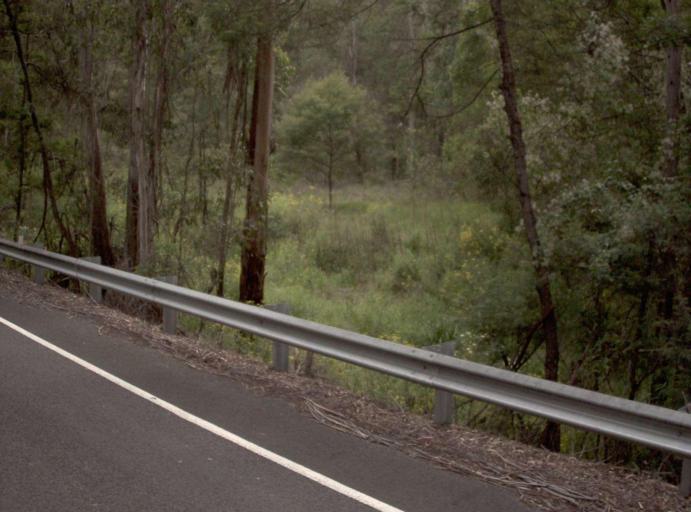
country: AU
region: New South Wales
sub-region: Bombala
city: Bombala
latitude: -37.4229
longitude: 149.2009
